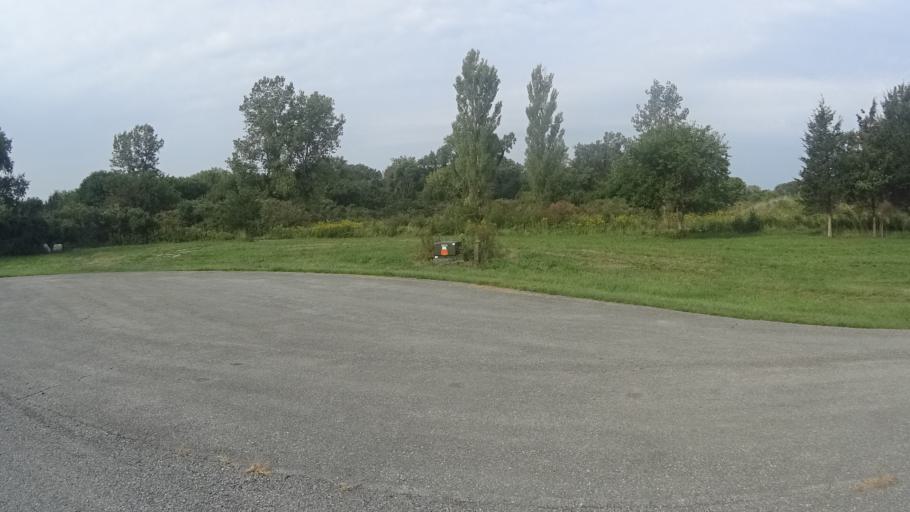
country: US
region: Ohio
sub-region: Erie County
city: Sandusky
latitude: 41.5913
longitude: -82.6962
